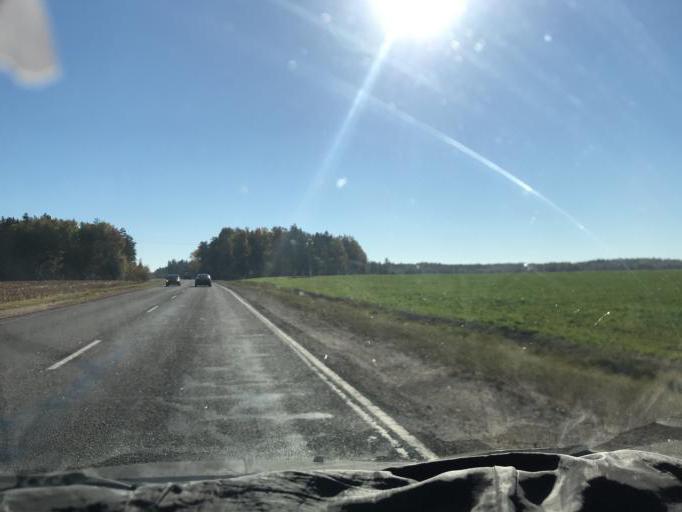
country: BY
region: Mogilev
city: Babruysk
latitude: 53.0599
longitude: 29.0859
